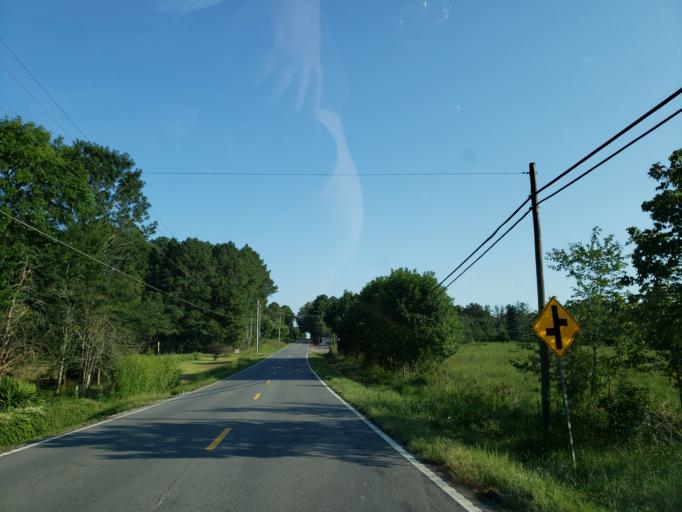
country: US
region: Tennessee
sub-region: Bradley County
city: Wildwood Lake
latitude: 35.0321
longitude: -84.8004
